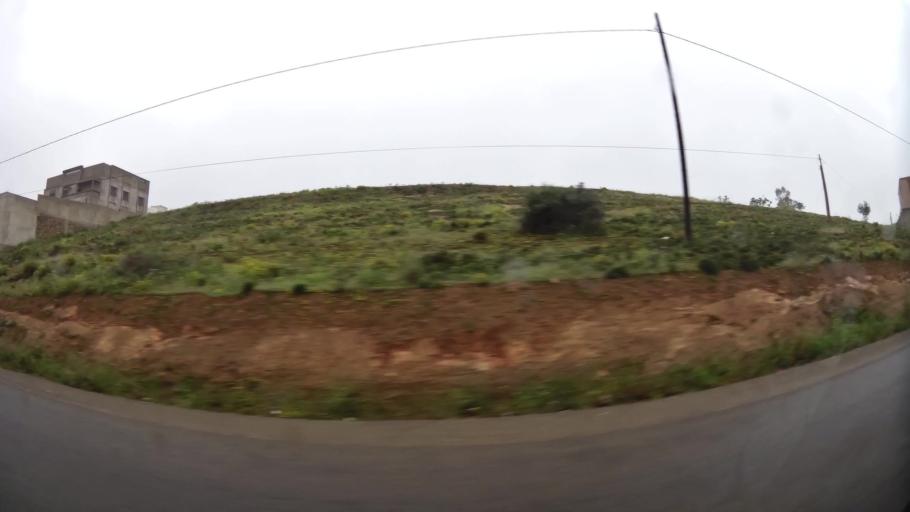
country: MA
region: Oriental
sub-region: Nador
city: Boudinar
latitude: 35.1287
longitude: -3.5827
